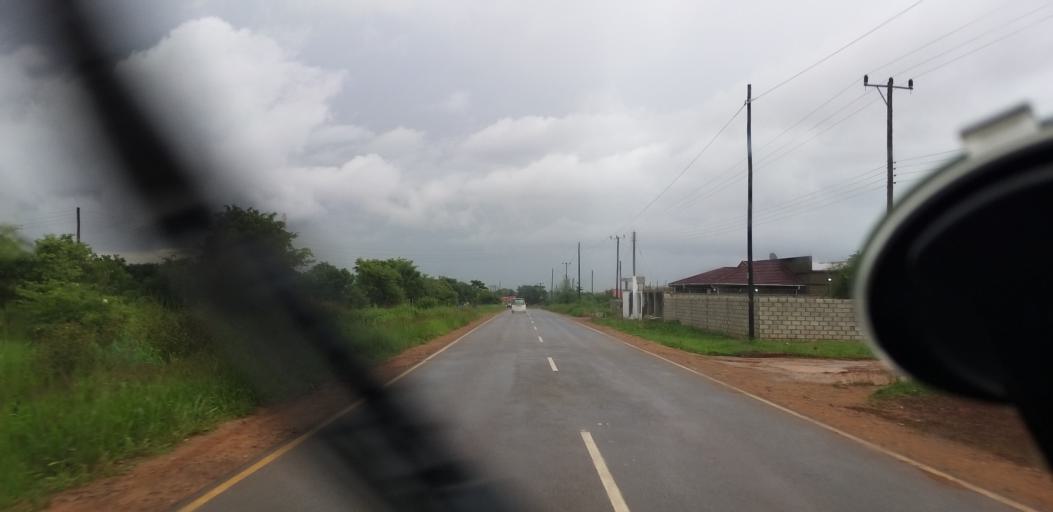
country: ZM
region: Lusaka
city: Lusaka
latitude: -15.4932
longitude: 28.3134
